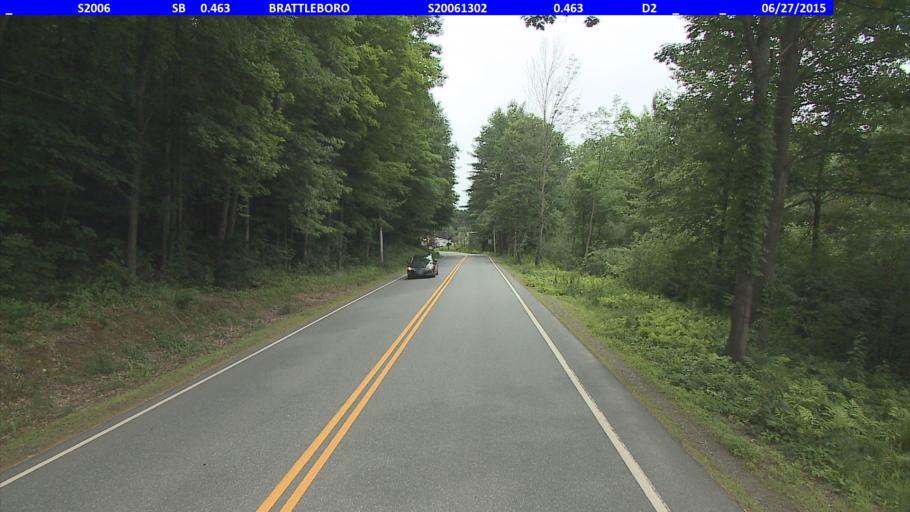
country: US
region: Vermont
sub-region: Windham County
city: Brattleboro
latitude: 42.8589
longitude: -72.5682
